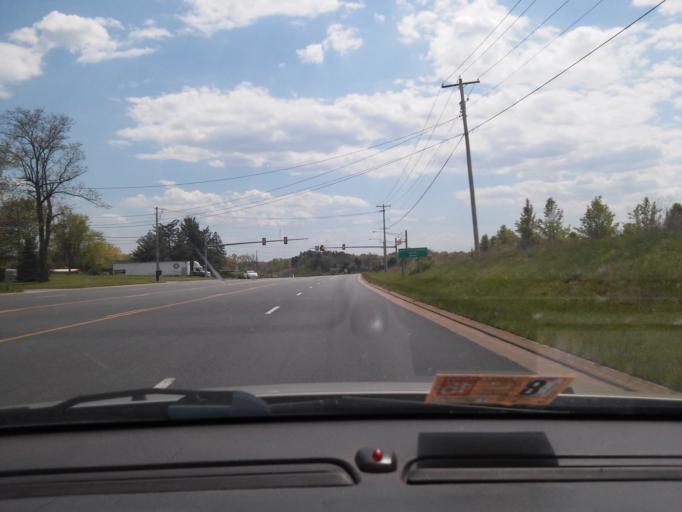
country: US
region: Virginia
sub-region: City of Winchester
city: Winchester
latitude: 39.1459
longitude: -78.1606
